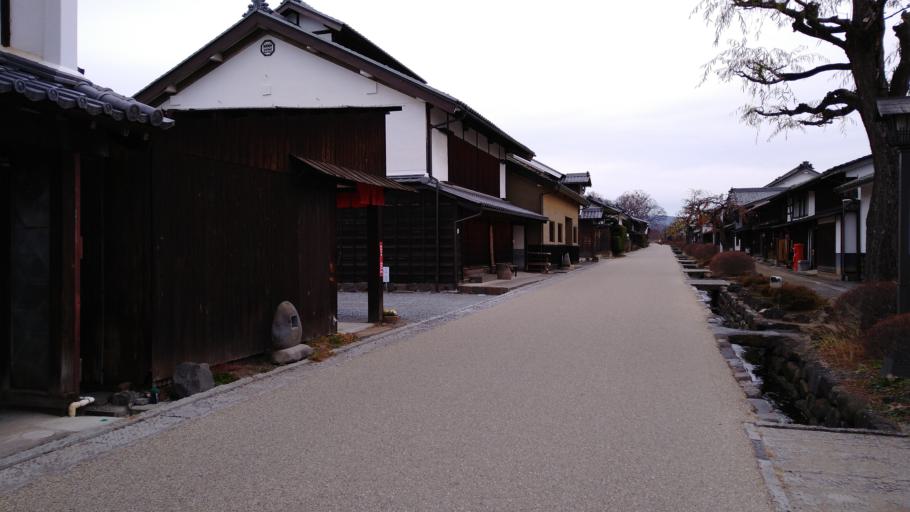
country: JP
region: Nagano
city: Ueda
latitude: 36.3619
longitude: 138.3130
